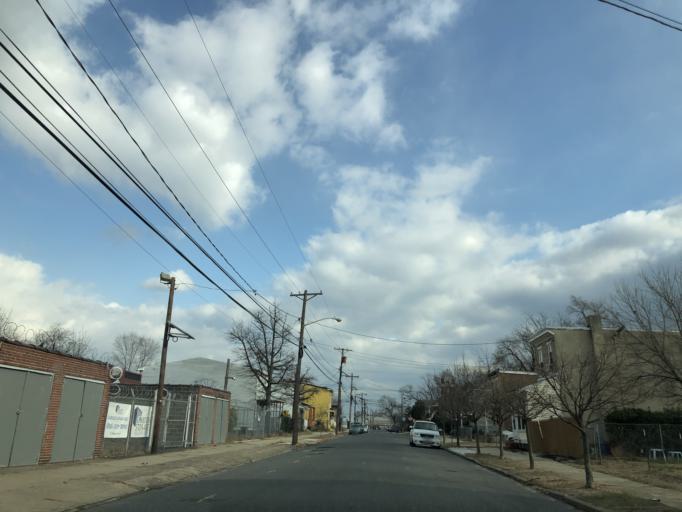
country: US
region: New Jersey
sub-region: Camden County
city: Camden
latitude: 39.9155
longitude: -75.1137
